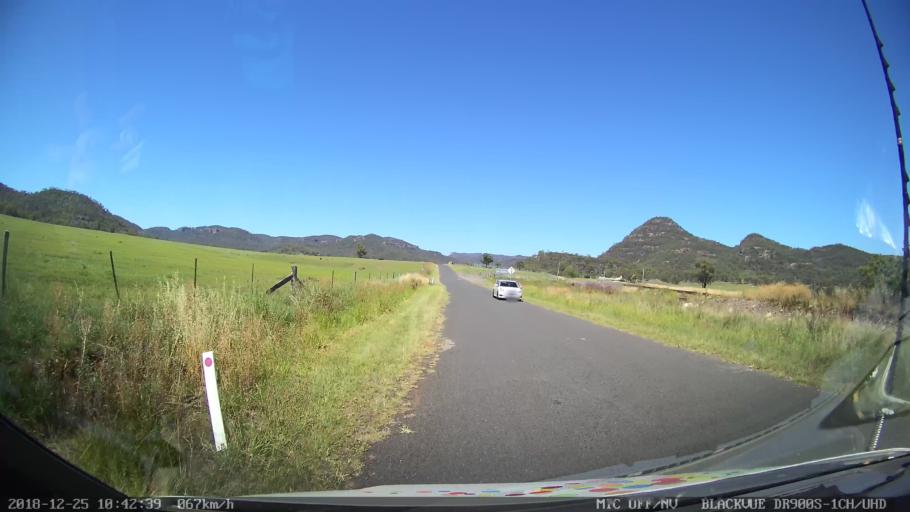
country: AU
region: New South Wales
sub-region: Upper Hunter Shire
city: Merriwa
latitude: -32.4169
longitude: 150.3208
